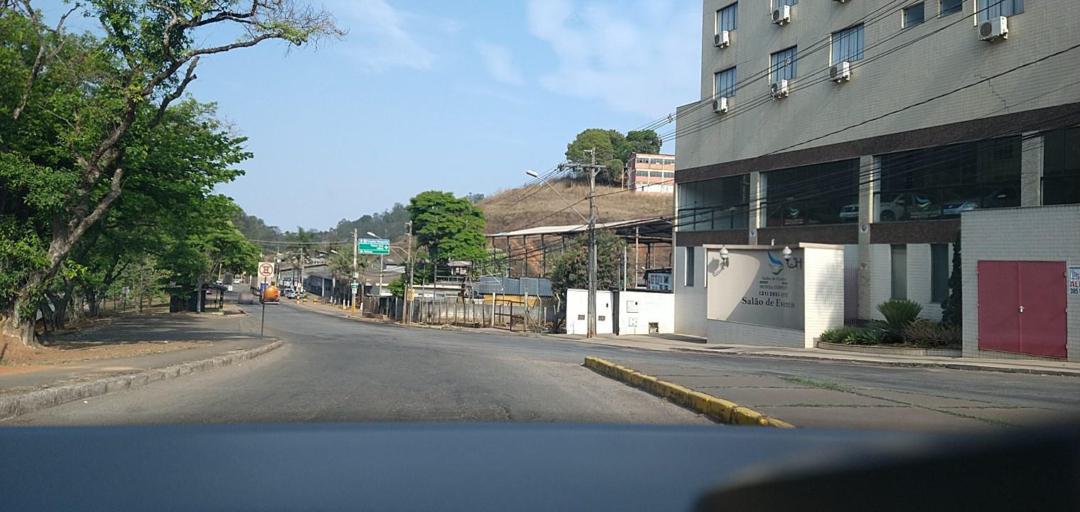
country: BR
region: Minas Gerais
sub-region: Joao Monlevade
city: Joao Monlevade
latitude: -19.8155
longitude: -43.1542
